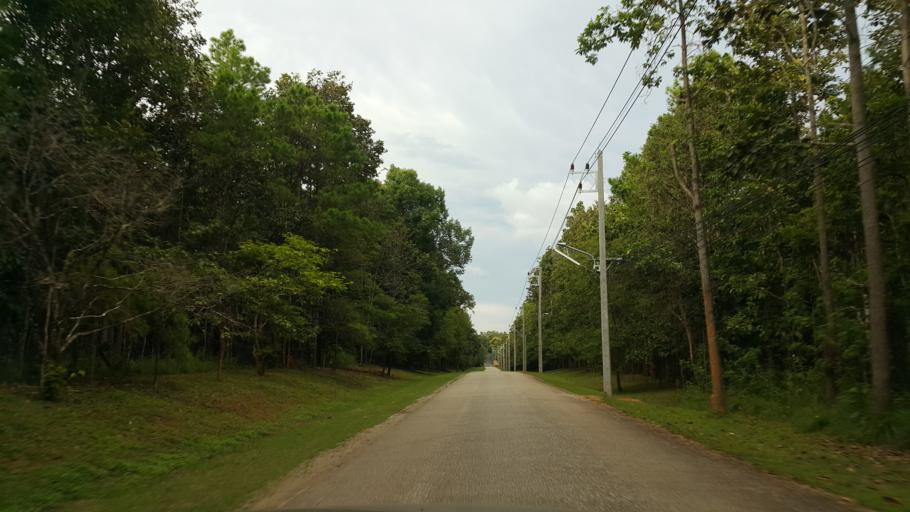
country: TH
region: Chiang Mai
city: Mae On
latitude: 18.8932
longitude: 99.2215
